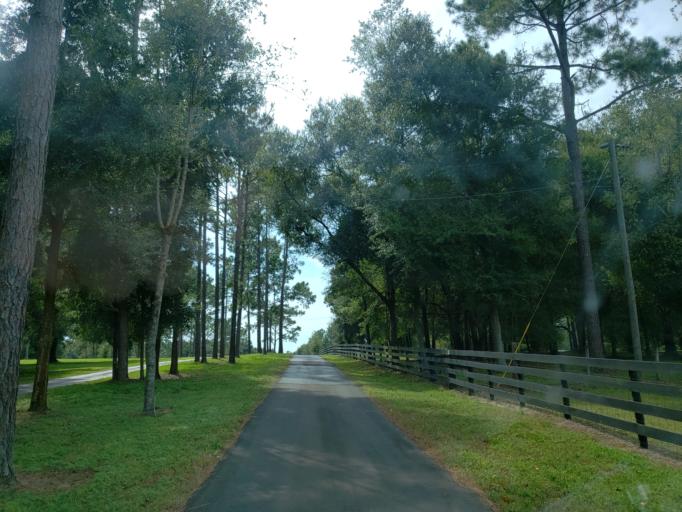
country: US
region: Florida
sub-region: Hernando County
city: Hill 'n Dale
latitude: 28.4587
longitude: -82.2676
